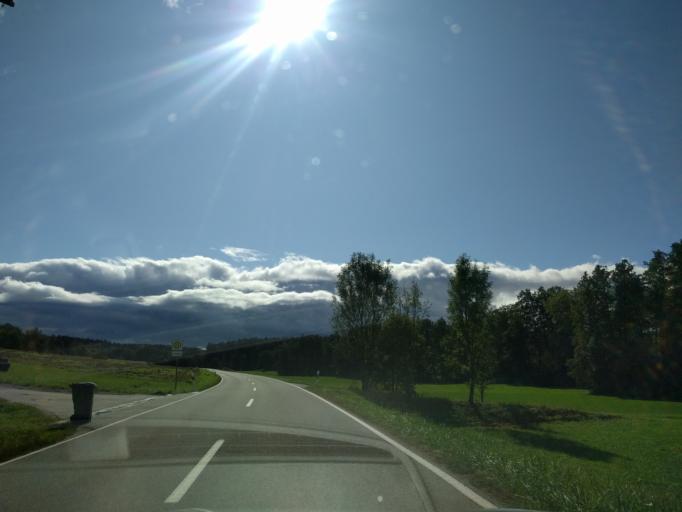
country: DE
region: Bavaria
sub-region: Lower Bavaria
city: Hengersberg
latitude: 48.8082
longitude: 13.0472
